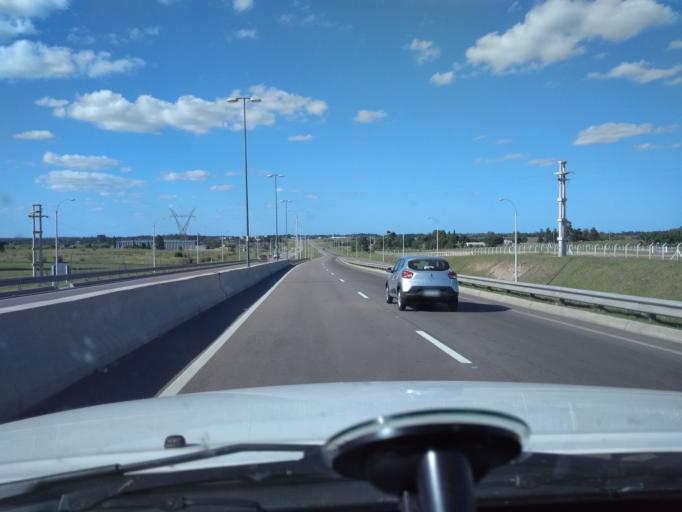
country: UY
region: Canelones
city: Las Piedras
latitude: -34.7199
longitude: -56.2456
